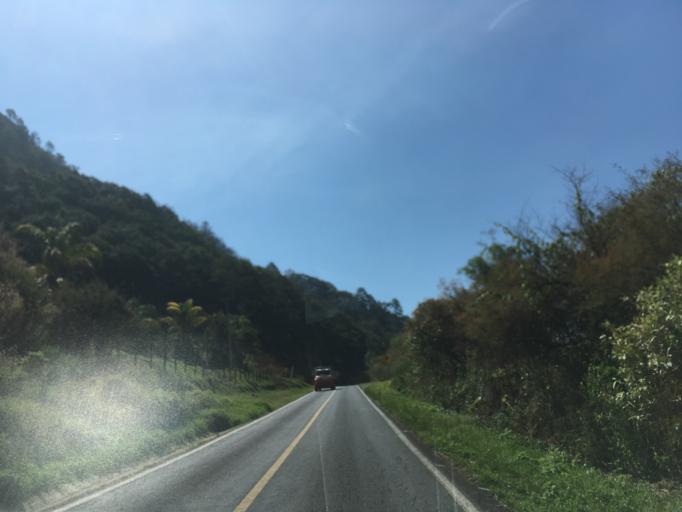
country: MX
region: Michoacan
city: Tzitzio
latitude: 19.6523
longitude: -100.9741
